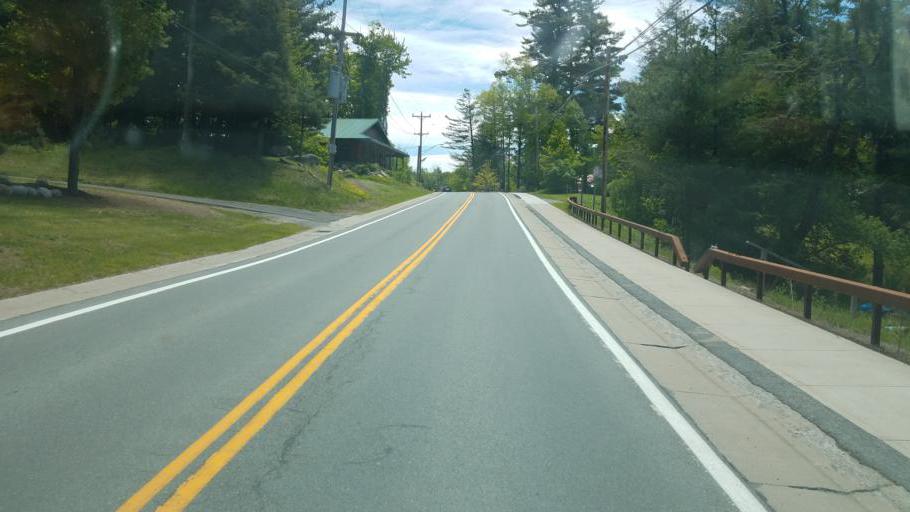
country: US
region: New York
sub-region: Hamilton County
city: Lake Pleasant
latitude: 43.7489
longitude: -74.7908
